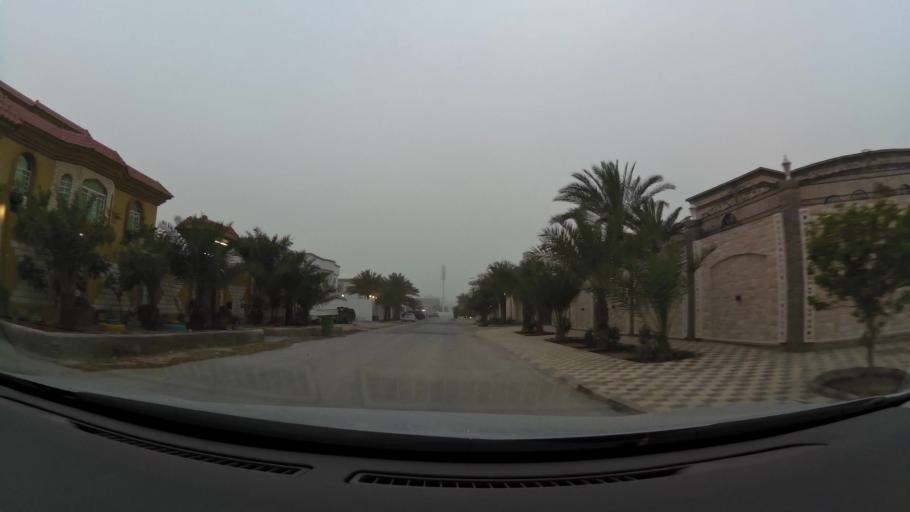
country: QA
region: Baladiyat ad Dawhah
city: Doha
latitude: 25.2279
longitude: 51.4972
